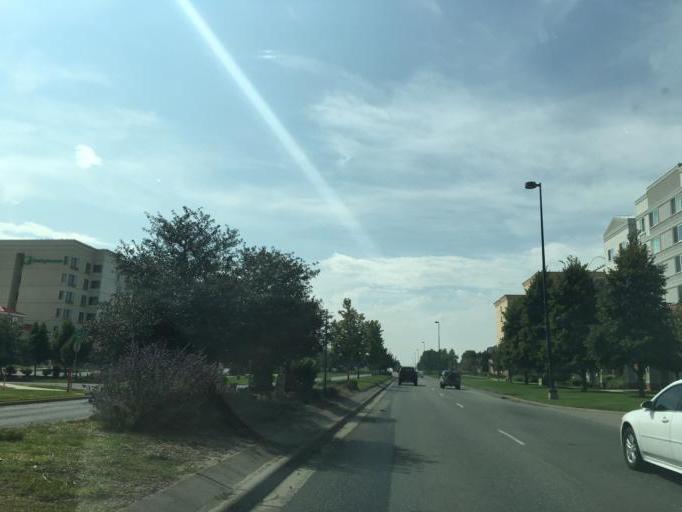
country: US
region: Colorado
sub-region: Adams County
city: Aurora
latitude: 39.8240
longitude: -104.7720
